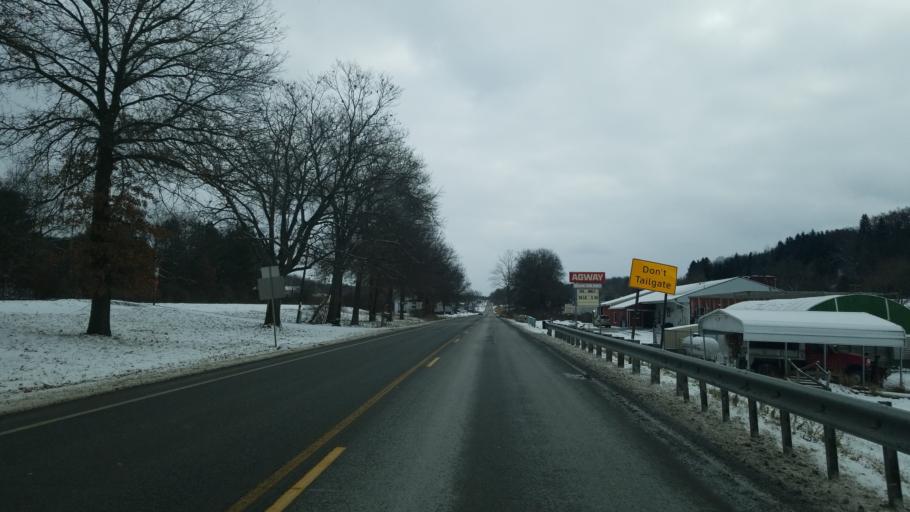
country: US
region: Pennsylvania
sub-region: Clearfield County
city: Sandy
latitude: 41.0907
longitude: -78.7701
